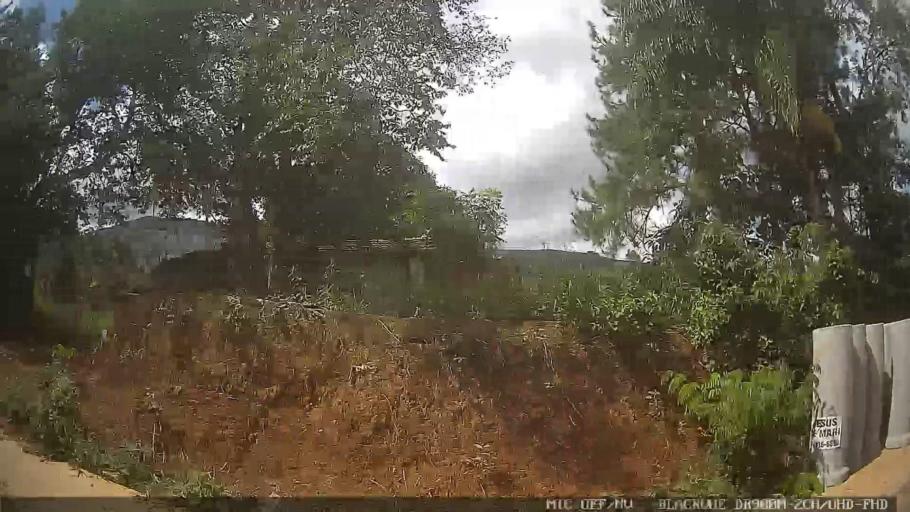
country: BR
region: Minas Gerais
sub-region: Extrema
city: Extrema
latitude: -22.8695
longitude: -46.3408
